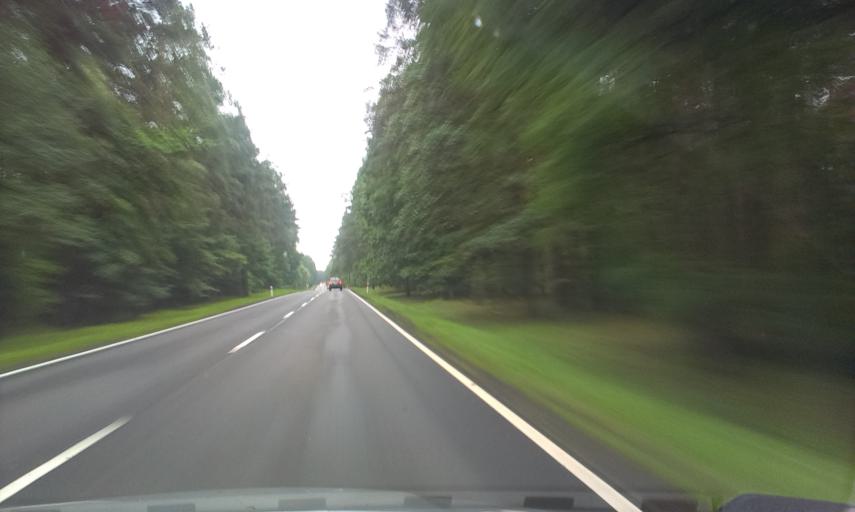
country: PL
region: Greater Poland Voivodeship
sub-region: Powiat zlotowski
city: Tarnowka
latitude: 53.2887
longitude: 16.7821
